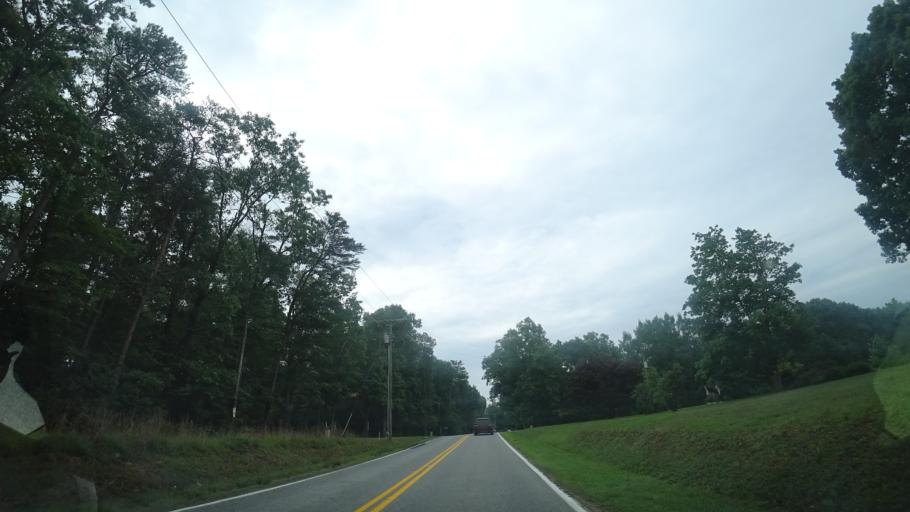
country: US
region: Virginia
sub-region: Spotsylvania County
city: Spotsylvania
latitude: 38.1272
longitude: -77.7787
